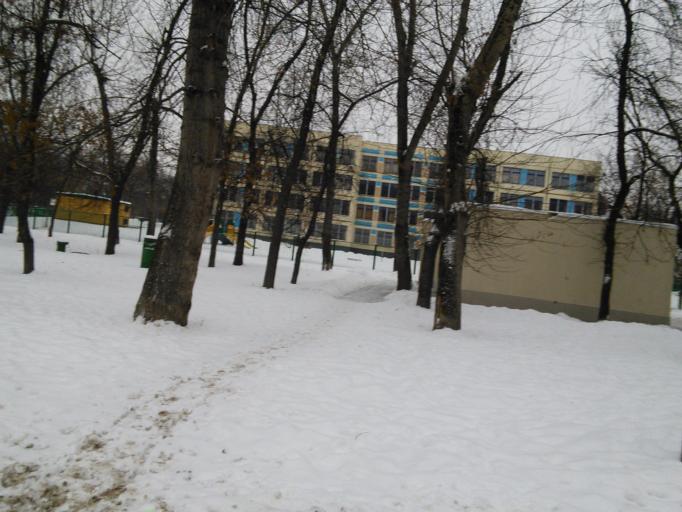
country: RU
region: Moscow
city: Lefortovo
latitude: 55.7641
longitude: 37.7067
